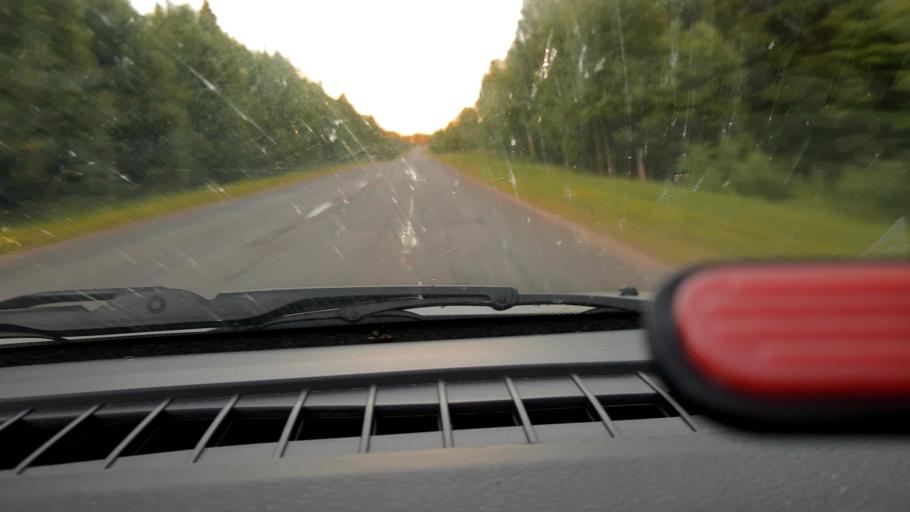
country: RU
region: Nizjnij Novgorod
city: Tonkino
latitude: 57.3466
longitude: 46.4552
